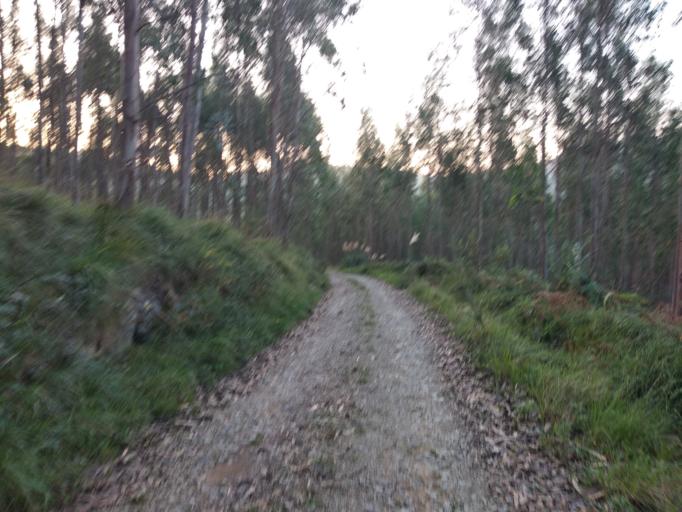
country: ES
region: Cantabria
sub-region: Provincia de Cantabria
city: Entrambasaguas
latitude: 43.3264
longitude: -3.6831
